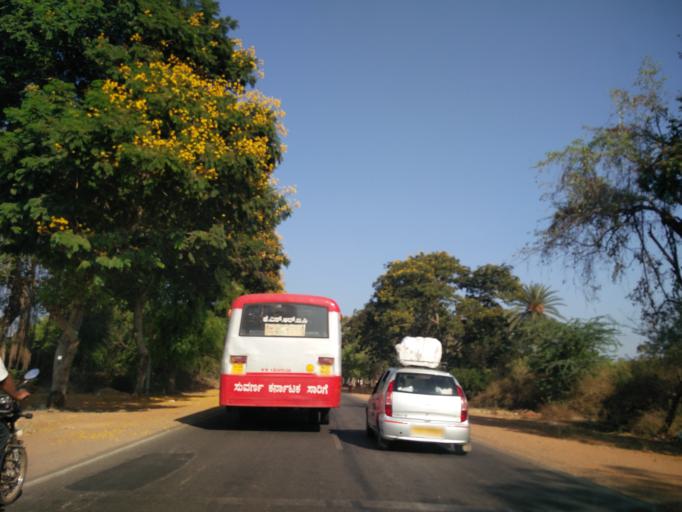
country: IN
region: Karnataka
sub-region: Tumkur
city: Gubbi
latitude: 13.3095
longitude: 76.9230
